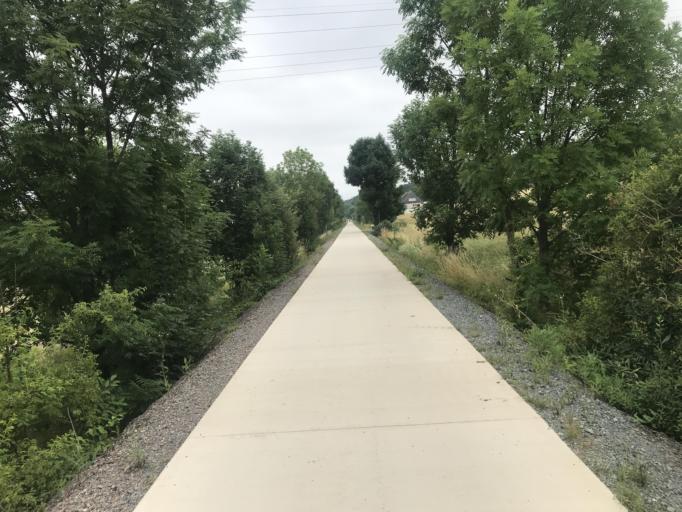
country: DE
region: Saxony-Anhalt
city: Rieder
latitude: 51.7306
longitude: 11.1588
